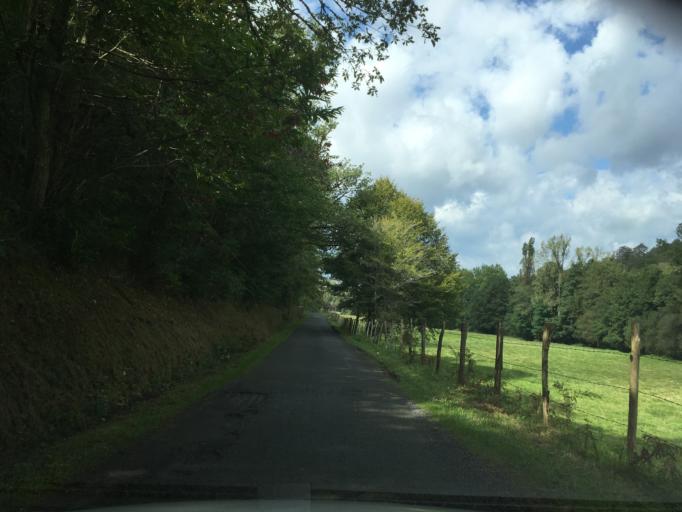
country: FR
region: Limousin
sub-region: Departement de la Correze
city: Brive-la-Gaillarde
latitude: 45.1257
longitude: 1.5343
